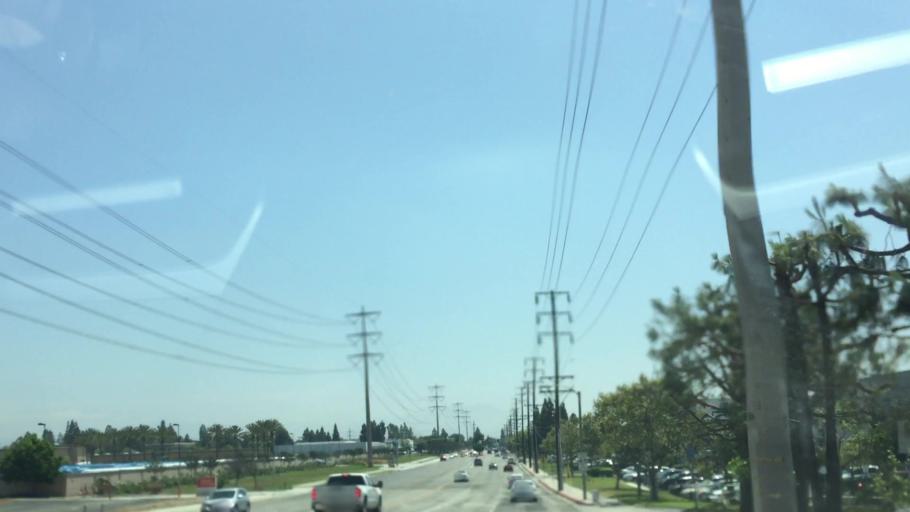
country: US
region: California
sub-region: Orange County
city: Fountain Valley
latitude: 33.7019
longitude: -117.9287
